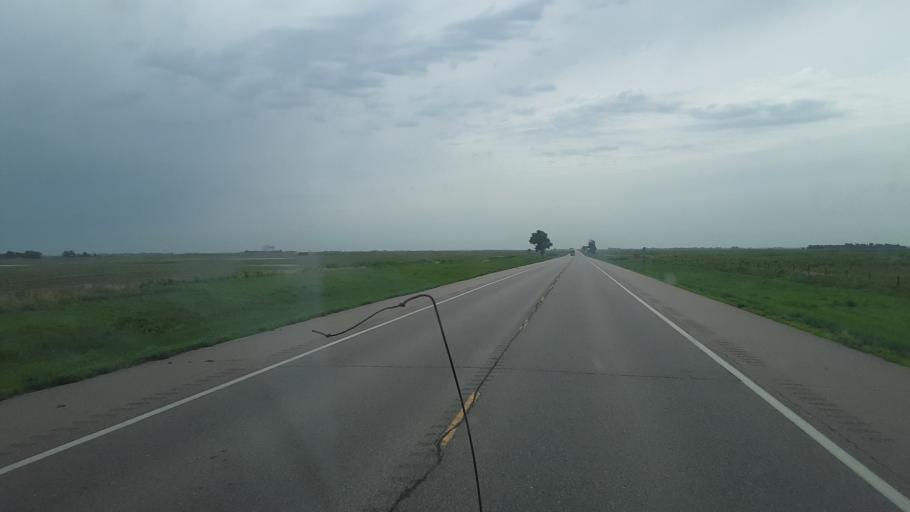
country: US
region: Kansas
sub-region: Stafford County
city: Saint John
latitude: 37.9563
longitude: -98.9258
